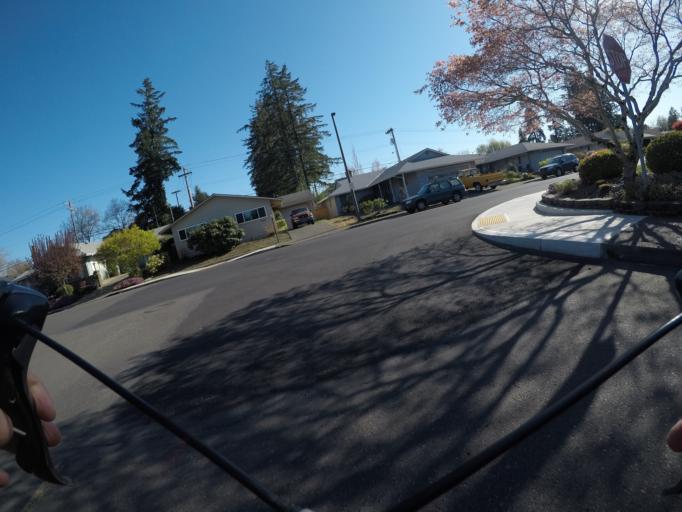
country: US
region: Oregon
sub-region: Washington County
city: King City
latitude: 45.3985
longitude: -122.8030
